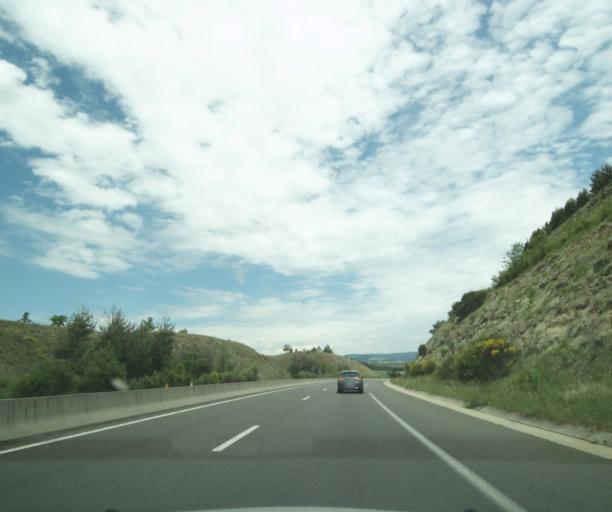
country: FR
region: Languedoc-Roussillon
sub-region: Departement de la Lozere
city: Chirac
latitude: 44.5248
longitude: 3.2414
